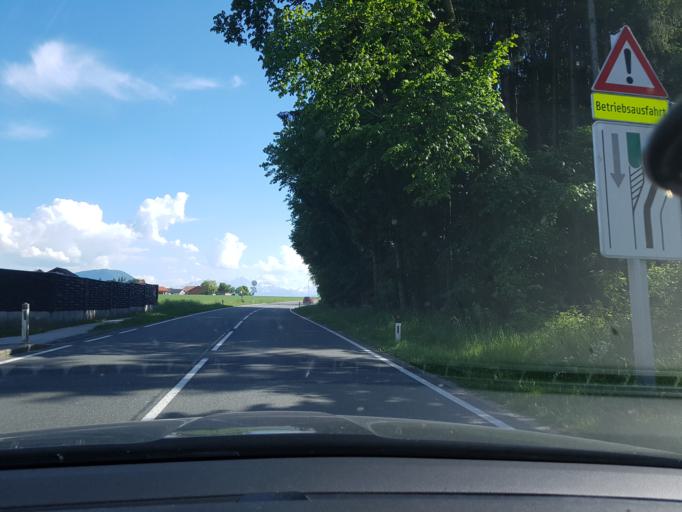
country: AT
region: Salzburg
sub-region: Politischer Bezirk Salzburg-Umgebung
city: Obertrum am See
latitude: 47.9087
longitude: 13.0813
